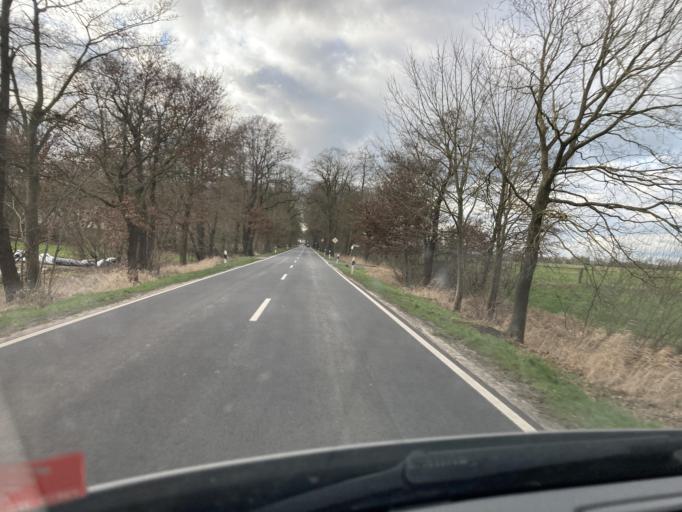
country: DE
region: Lower Saxony
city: Filsum
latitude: 53.1869
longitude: 7.6064
